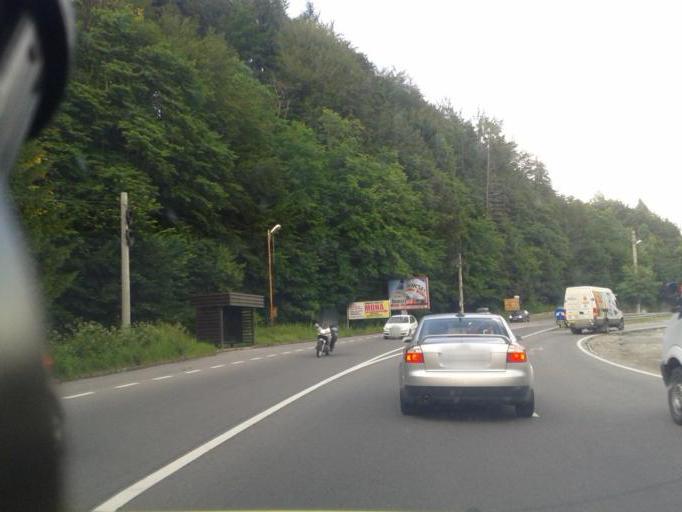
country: RO
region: Prahova
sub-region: Oras Busteni
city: Poiana Tapului
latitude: 45.3861
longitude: 25.5376
